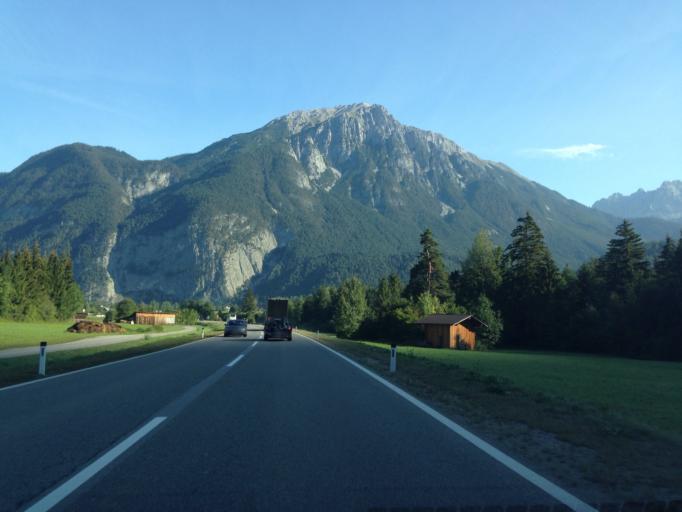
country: AT
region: Tyrol
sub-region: Politischer Bezirk Imst
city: Nassereith
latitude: 47.2973
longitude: 10.8435
